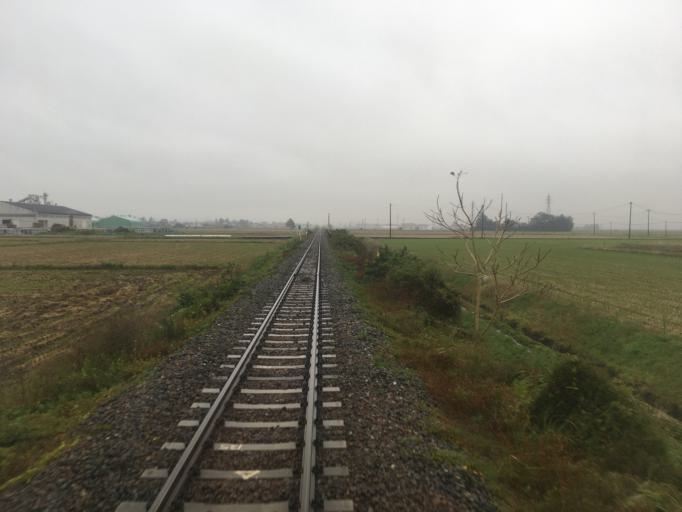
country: JP
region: Miyagi
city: Furukawa
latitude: 38.5645
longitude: 141.0026
